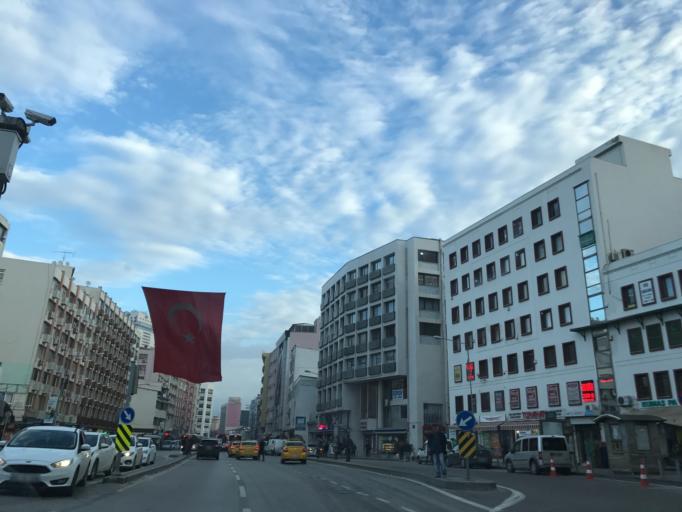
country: TR
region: Izmir
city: Izmir
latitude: 38.4203
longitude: 27.1370
